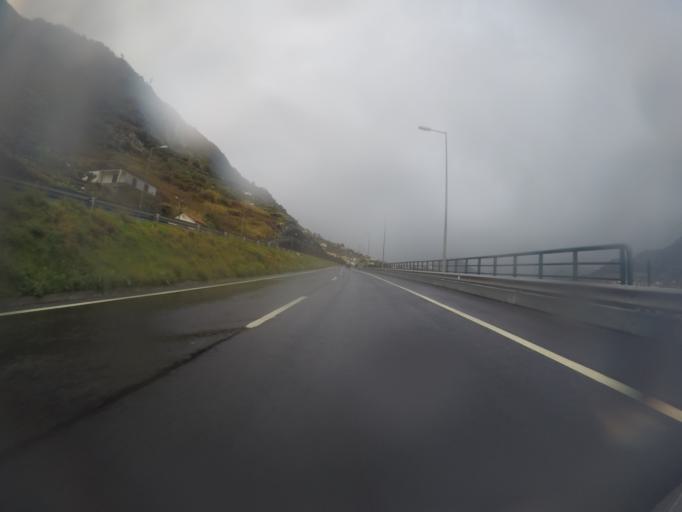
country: PT
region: Madeira
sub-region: Machico
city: Machico
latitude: 32.7186
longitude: -16.7718
